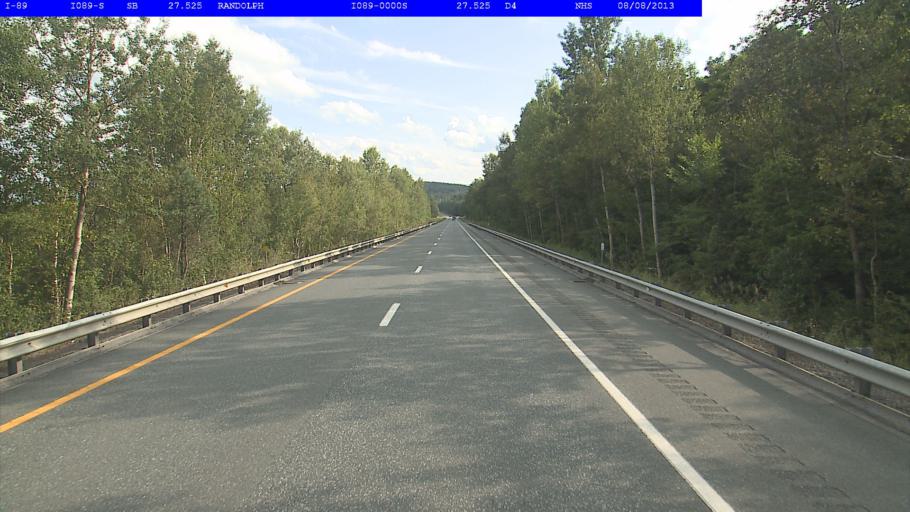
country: US
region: Vermont
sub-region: Orange County
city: Randolph
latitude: 43.8976
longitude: -72.6162
